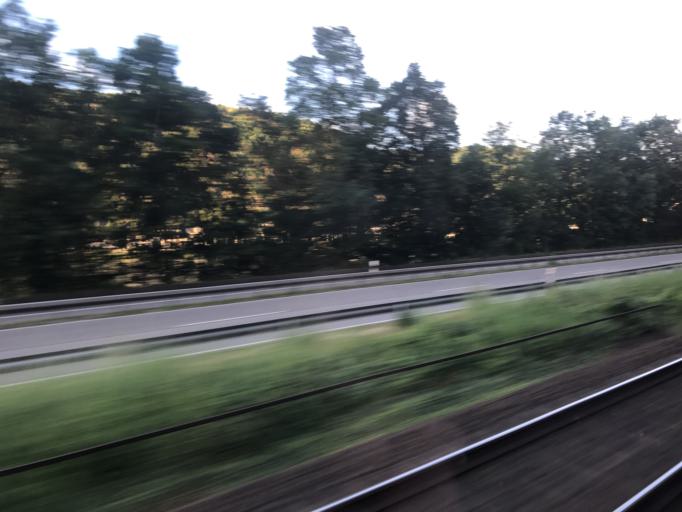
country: DE
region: Rheinland-Pfalz
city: Dorscheid
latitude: 50.0907
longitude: 7.7507
